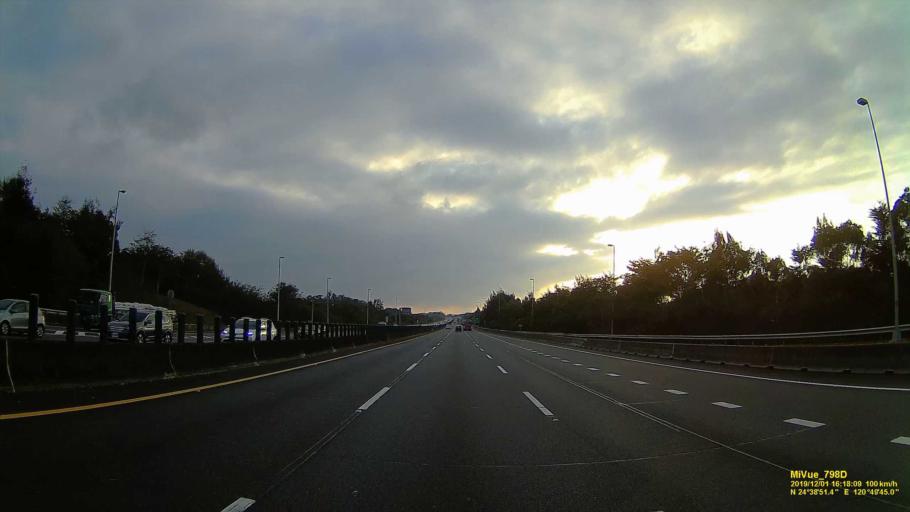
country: TW
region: Taiwan
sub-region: Miaoli
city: Miaoli
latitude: 24.6473
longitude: 120.8287
